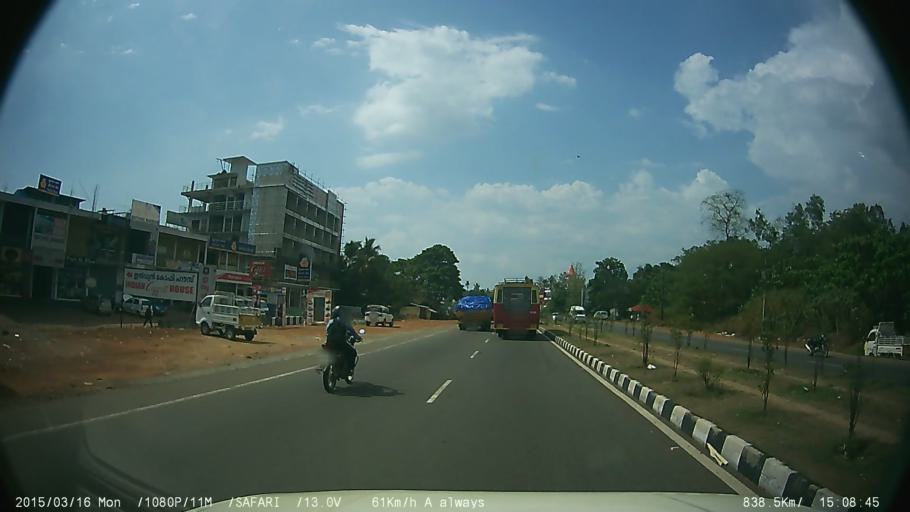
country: IN
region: Kerala
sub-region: Thrissur District
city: Kizhake Chalakudi
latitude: 10.2716
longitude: 76.3477
